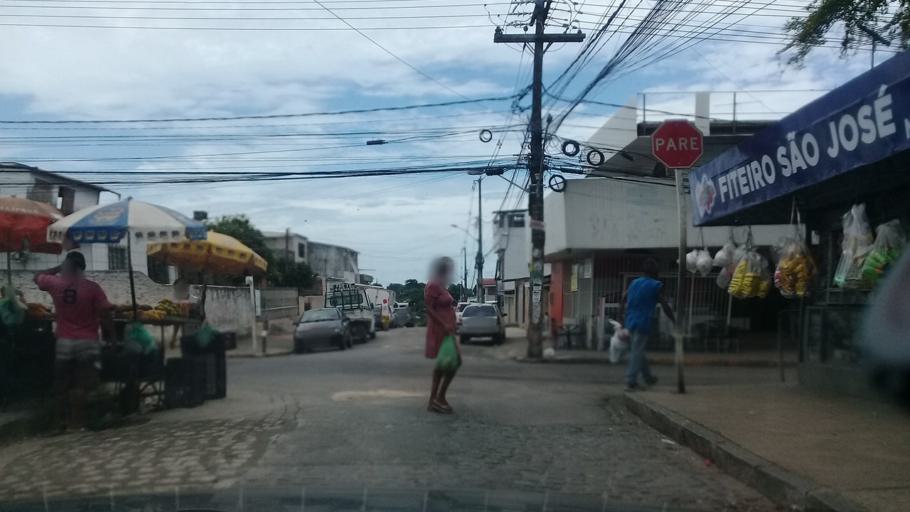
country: BR
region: Pernambuco
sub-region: Jaboatao Dos Guararapes
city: Jaboatao dos Guararapes
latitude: -8.1186
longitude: -34.9549
